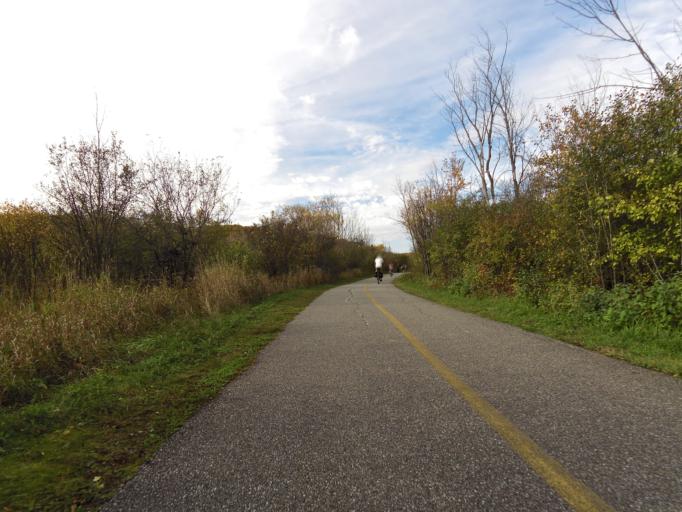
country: CA
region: Quebec
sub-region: Outaouais
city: Gatineau
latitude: 45.4625
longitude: -75.7869
